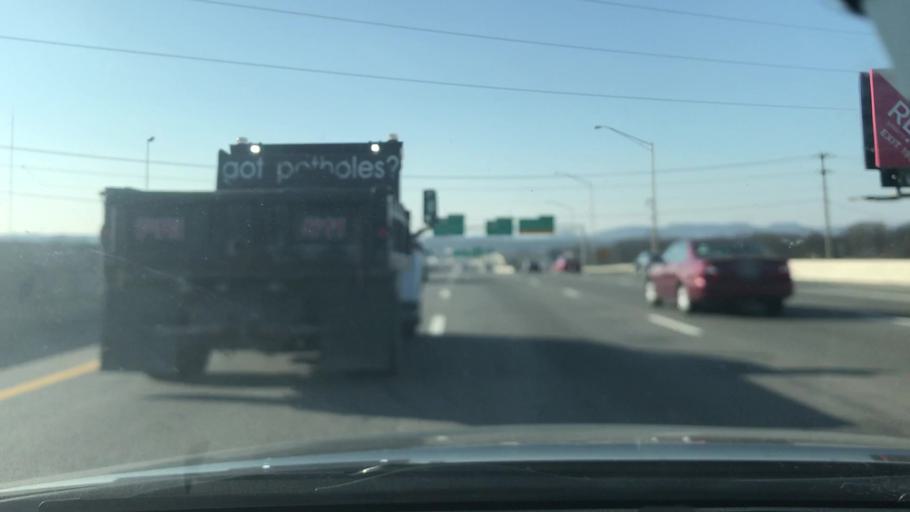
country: US
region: Tennessee
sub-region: Davidson County
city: Nashville
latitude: 36.1541
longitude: -86.8364
